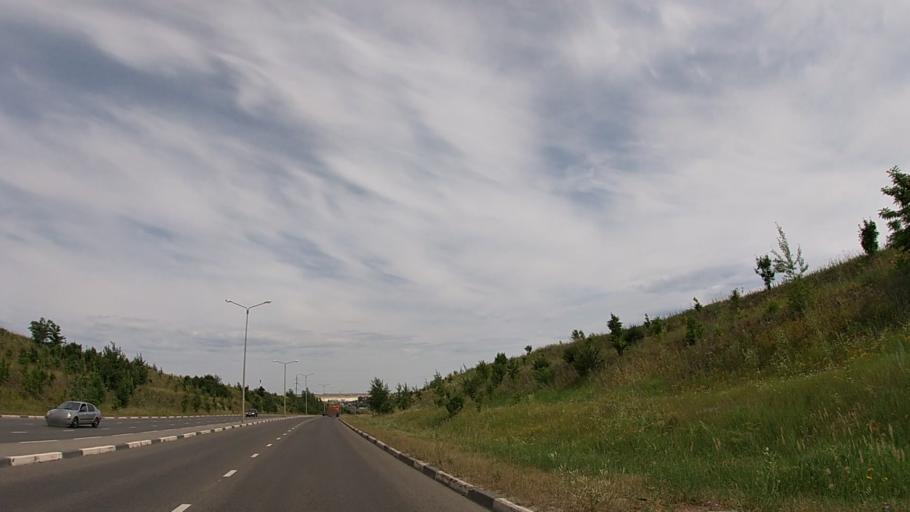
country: RU
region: Belgorod
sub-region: Belgorodskiy Rayon
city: Belgorod
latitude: 50.6022
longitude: 36.5299
